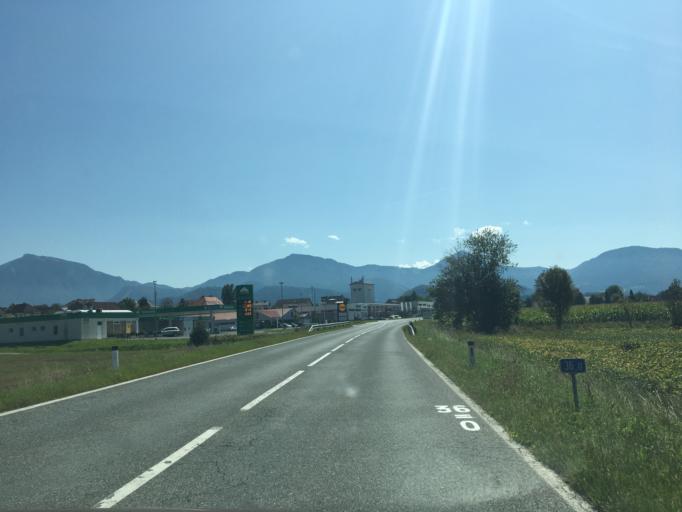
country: AT
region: Carinthia
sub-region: Politischer Bezirk Volkermarkt
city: Eberndorf
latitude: 46.5931
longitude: 14.6360
